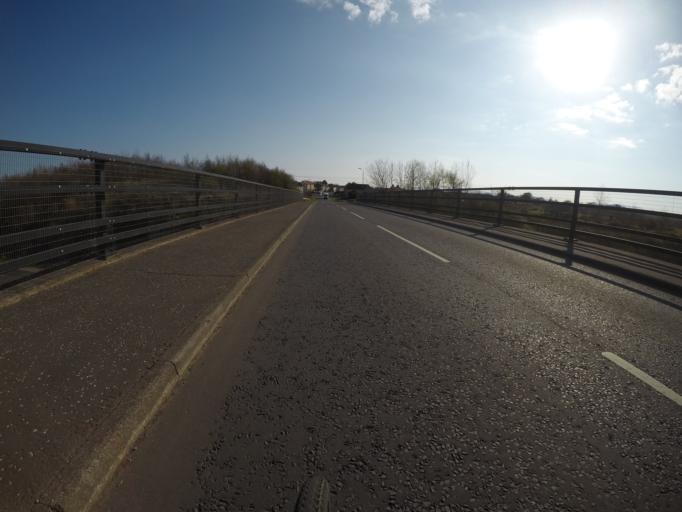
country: GB
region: Scotland
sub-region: North Ayrshire
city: Stevenston
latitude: 55.6514
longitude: -4.7415
